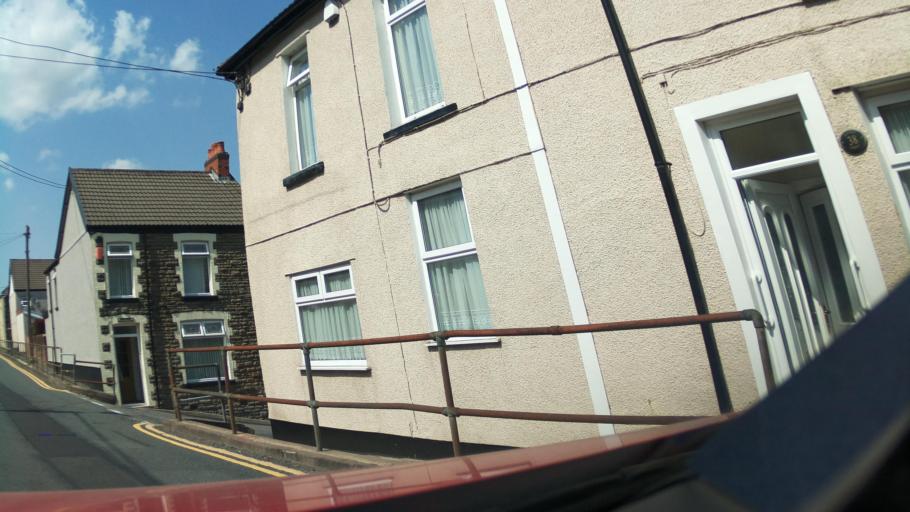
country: GB
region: Wales
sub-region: Caerphilly County Borough
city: Rhymney
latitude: 51.7425
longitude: -3.2776
